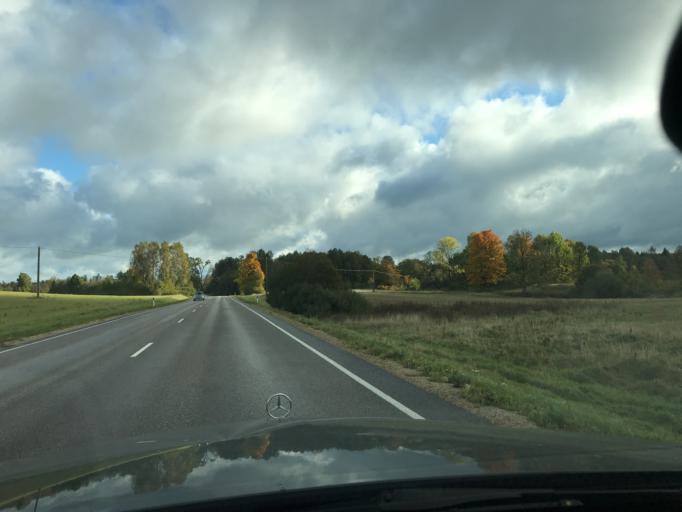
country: EE
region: Valgamaa
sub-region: Torva linn
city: Torva
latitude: 58.0184
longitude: 25.8046
